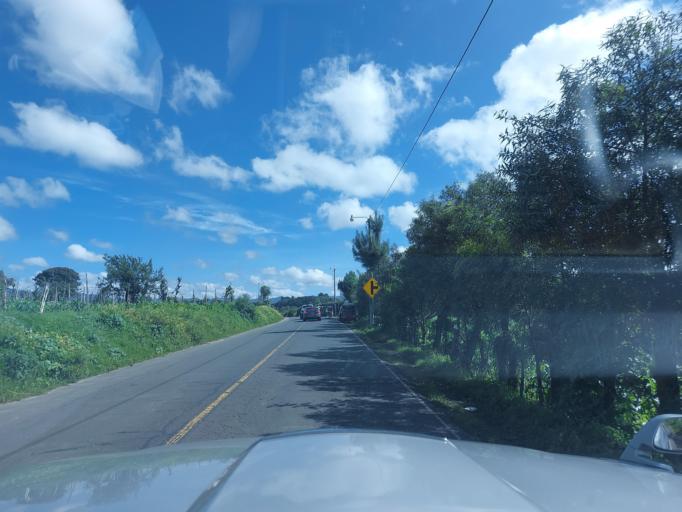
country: GT
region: Chimaltenango
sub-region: Municipio de Zaragoza
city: Zaragoza
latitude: 14.6601
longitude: -90.8978
